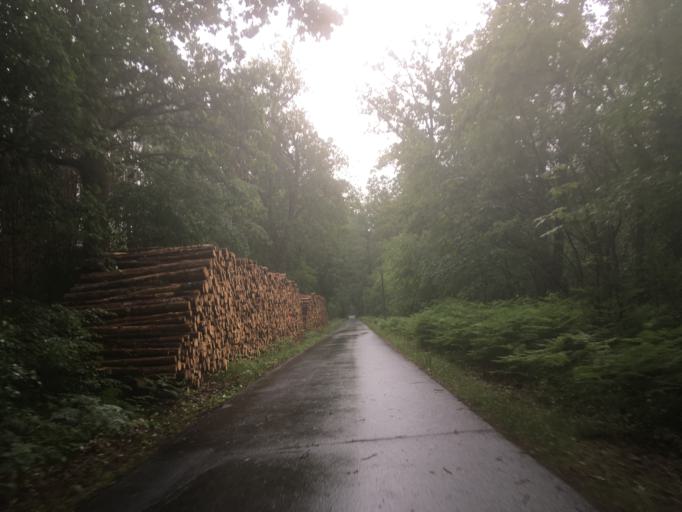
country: DE
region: Brandenburg
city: Liebenwalde
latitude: 52.8524
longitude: 13.4368
